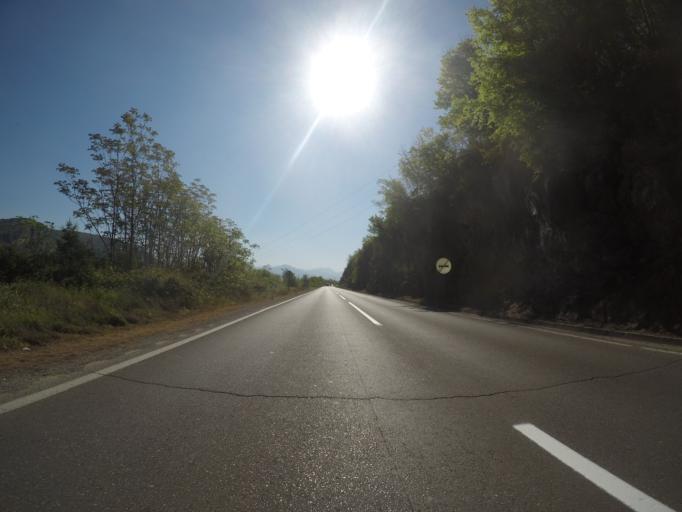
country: ME
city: Spuz
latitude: 42.4552
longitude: 19.1886
